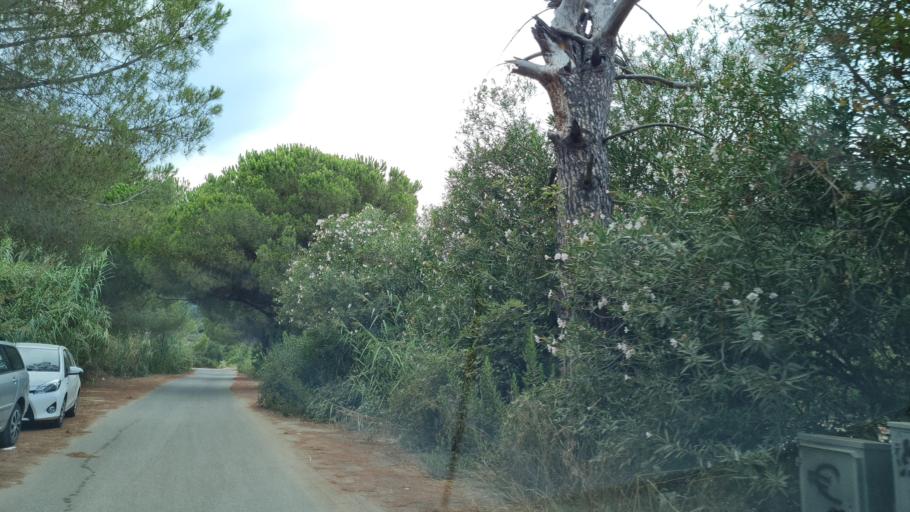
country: IT
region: Tuscany
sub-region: Provincia di Grosseto
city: Porto Ercole
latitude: 42.4036
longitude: 11.2053
